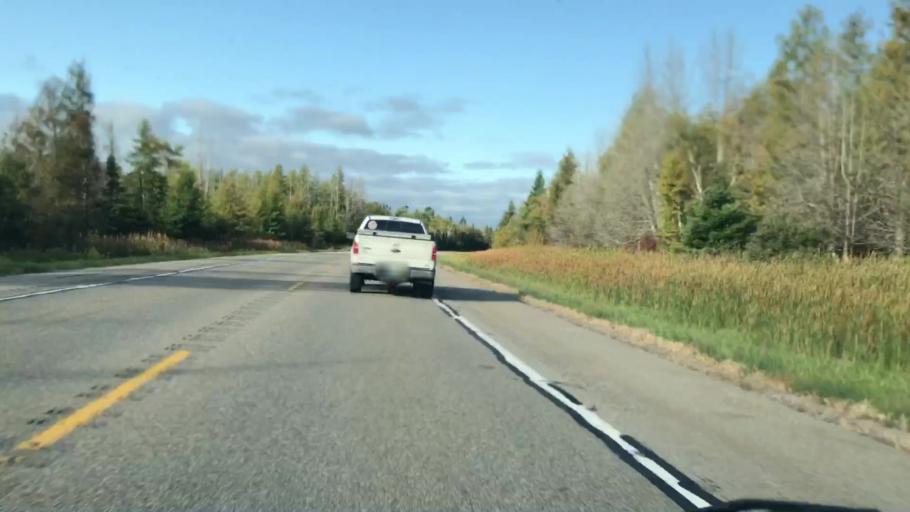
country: US
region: Michigan
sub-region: Luce County
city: Newberry
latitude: 46.3045
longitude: -85.2232
